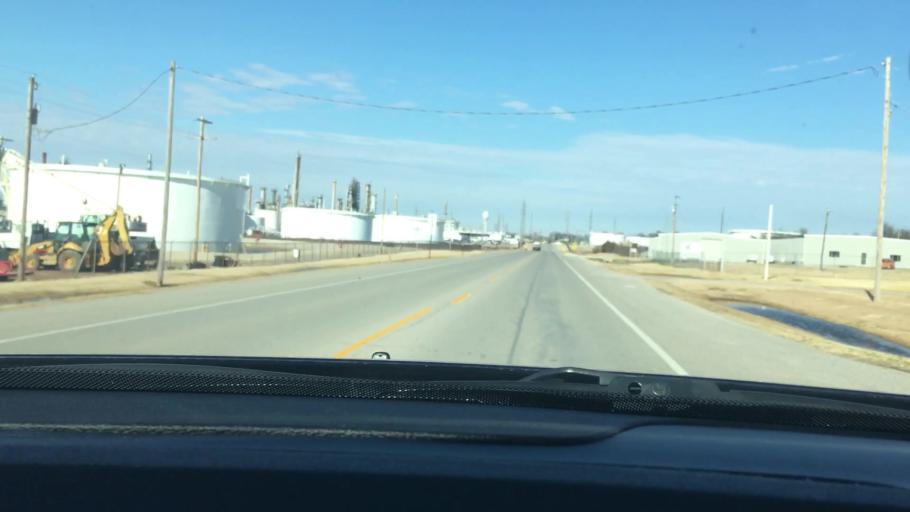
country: US
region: Oklahoma
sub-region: Garvin County
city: Wynnewood
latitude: 34.6265
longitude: -97.1640
